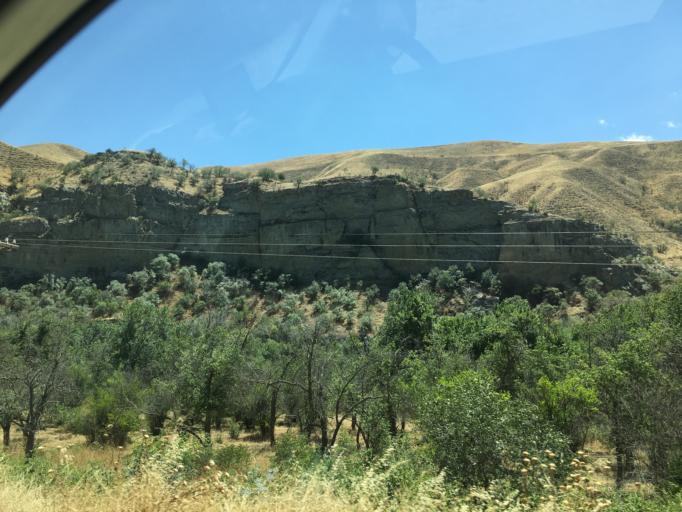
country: TM
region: Balkan
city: Magtymguly
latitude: 38.4173
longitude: 56.6783
